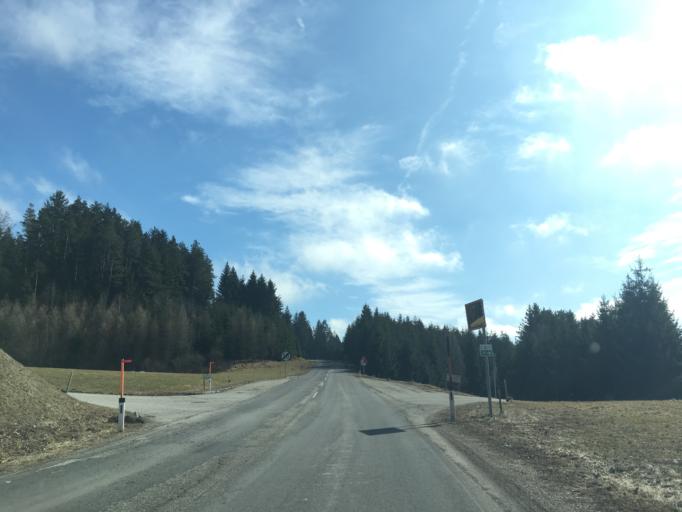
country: AT
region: Upper Austria
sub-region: Politischer Bezirk Perg
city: Sankt Georgen am Walde
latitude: 48.4011
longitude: 14.8500
